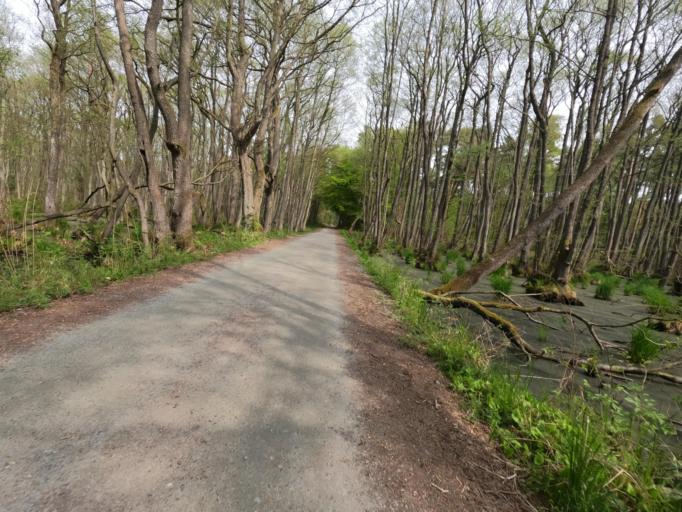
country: DE
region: Mecklenburg-Vorpommern
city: Ostseebad Prerow
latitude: 54.4572
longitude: 12.5132
